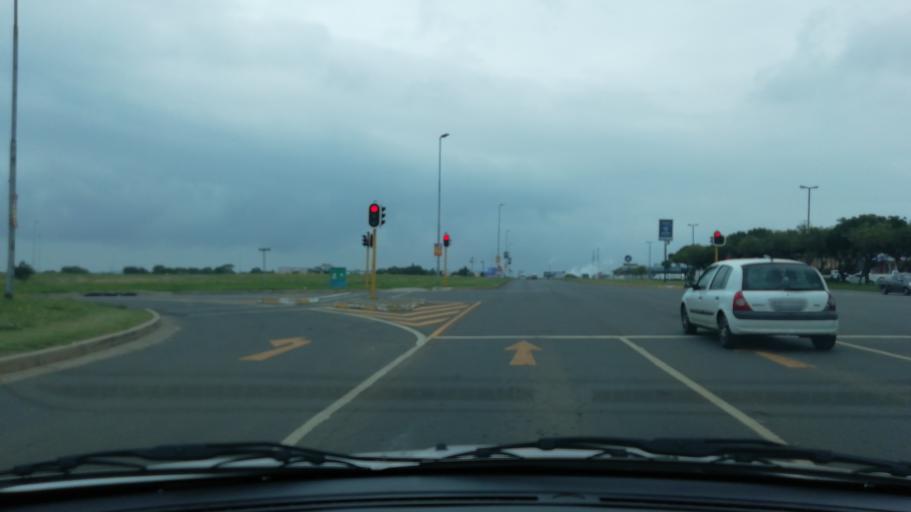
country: ZA
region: KwaZulu-Natal
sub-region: uThungulu District Municipality
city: Richards Bay
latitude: -28.7564
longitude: 32.0459
